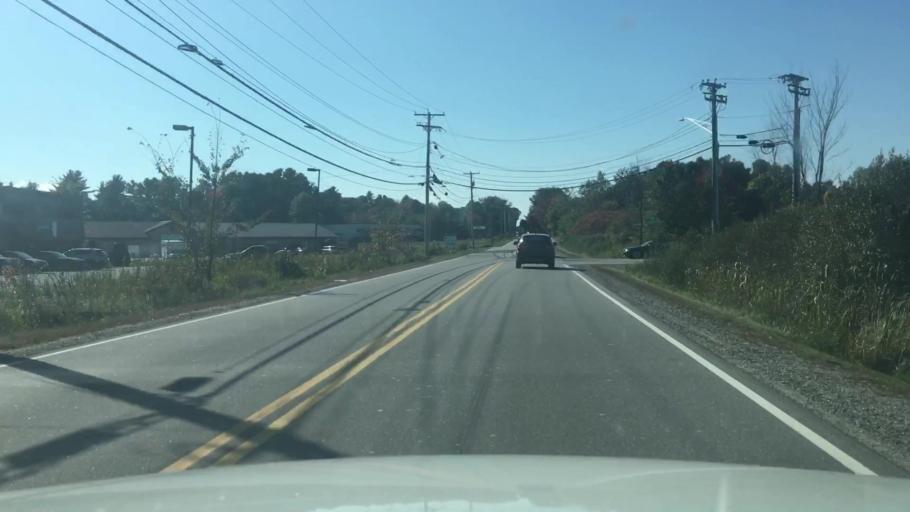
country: US
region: Maine
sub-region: Cumberland County
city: Westbrook
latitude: 43.6497
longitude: -70.3661
